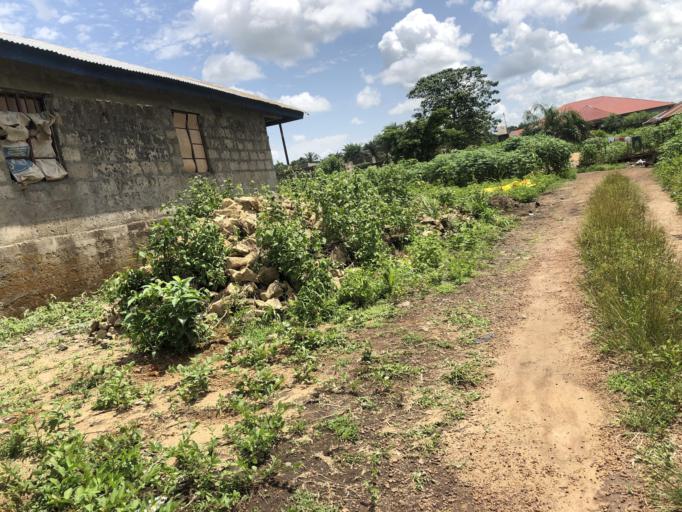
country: SL
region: Northern Province
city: Magburaka
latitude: 8.7118
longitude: -11.9284
